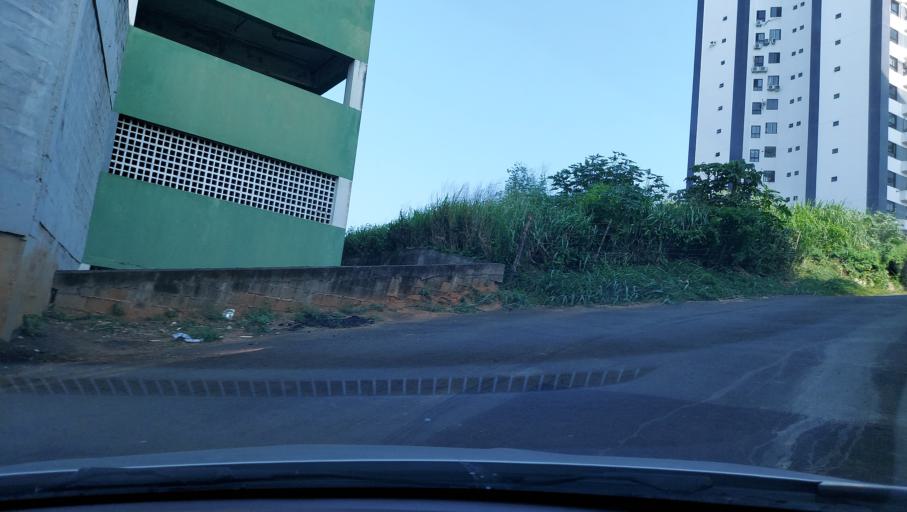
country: BR
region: Bahia
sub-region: Salvador
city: Salvador
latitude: -12.9849
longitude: -38.4682
